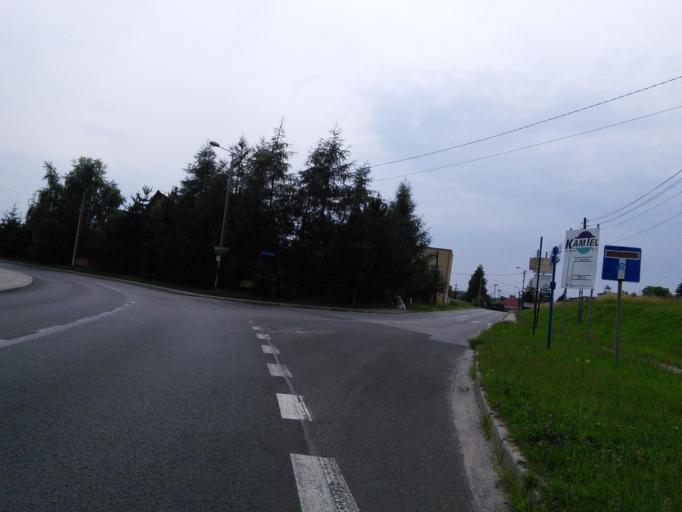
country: PL
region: Silesian Voivodeship
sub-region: Powiat bedzinski
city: Bobrowniki
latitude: 50.3757
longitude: 18.9642
